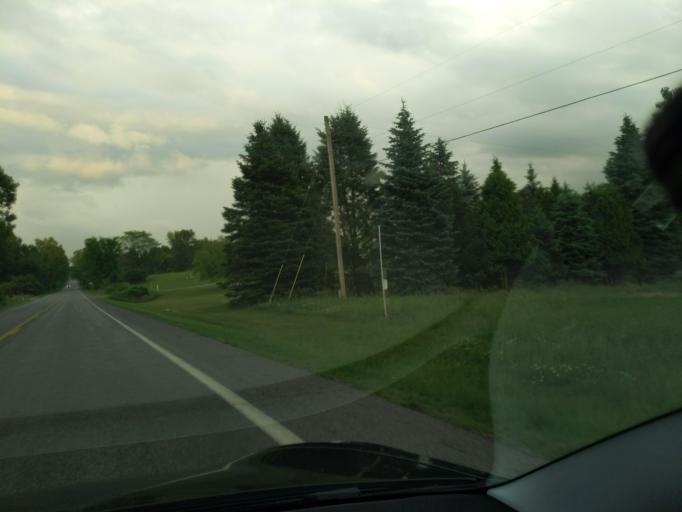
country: US
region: Michigan
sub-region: Ingham County
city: Mason
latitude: 42.5239
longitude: -84.3831
